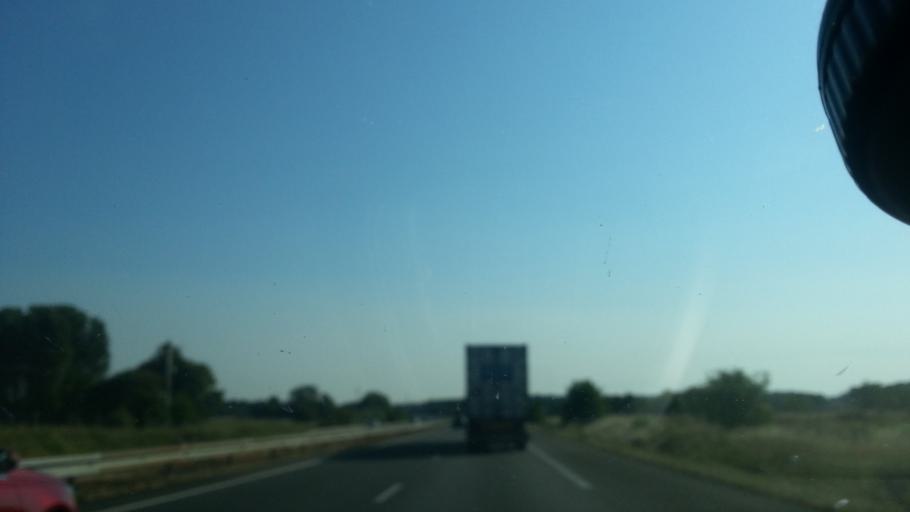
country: FR
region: Poitou-Charentes
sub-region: Departement de la Vienne
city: Naintre
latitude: 46.7721
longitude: 0.4858
